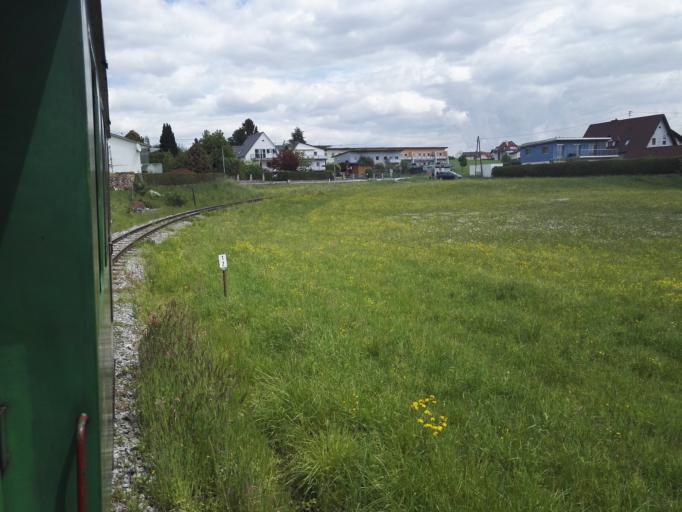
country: AT
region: Styria
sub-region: Politischer Bezirk Weiz
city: Krottendorf
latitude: 47.2154
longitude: 15.6394
